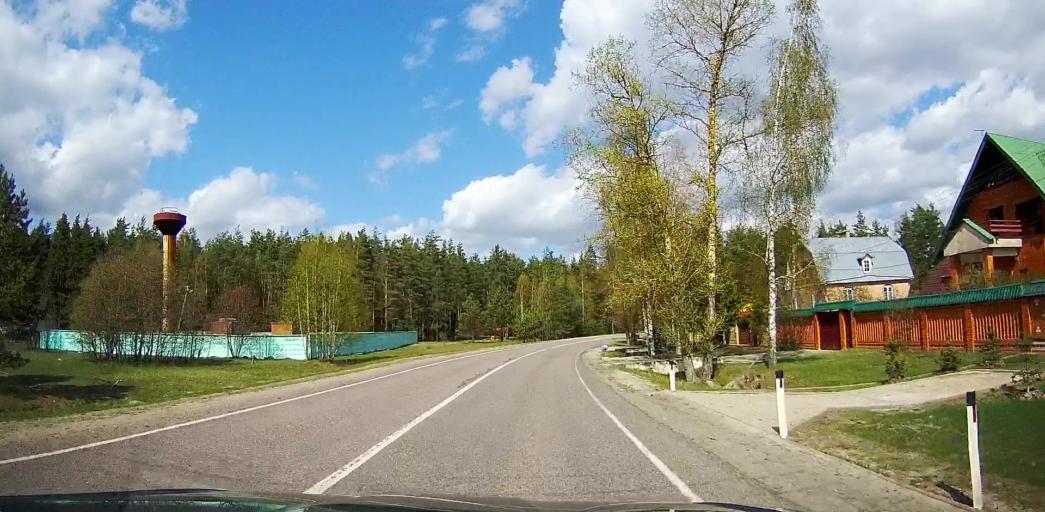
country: RU
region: Moskovskaya
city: Davydovo
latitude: 55.5622
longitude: 38.8132
